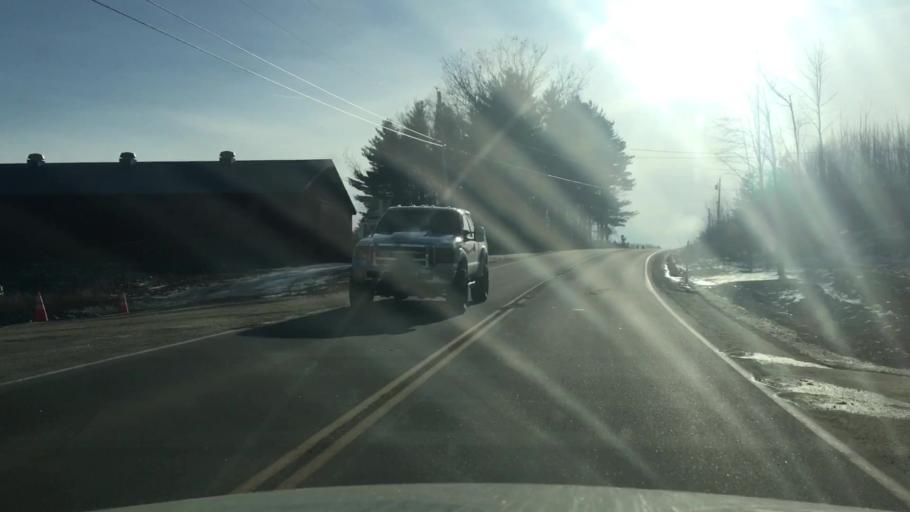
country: US
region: Maine
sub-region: Androscoggin County
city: Sabattus
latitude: 44.1197
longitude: -70.0864
